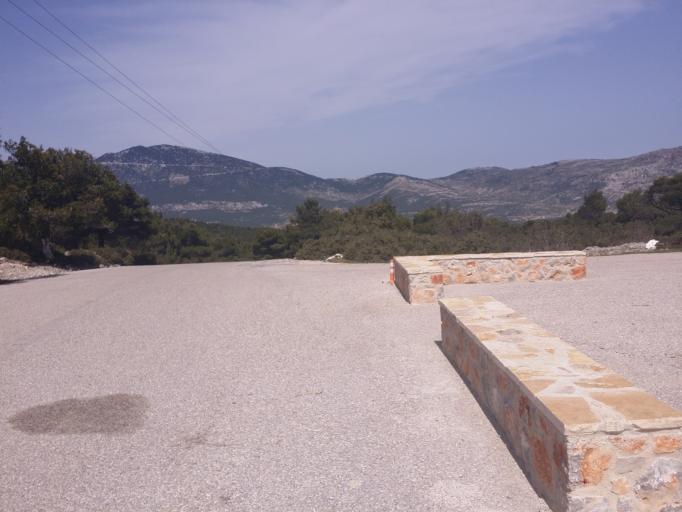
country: GR
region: Attica
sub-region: Nomarchia Dytikis Attikis
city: Vilia
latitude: 38.1387
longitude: 23.3157
